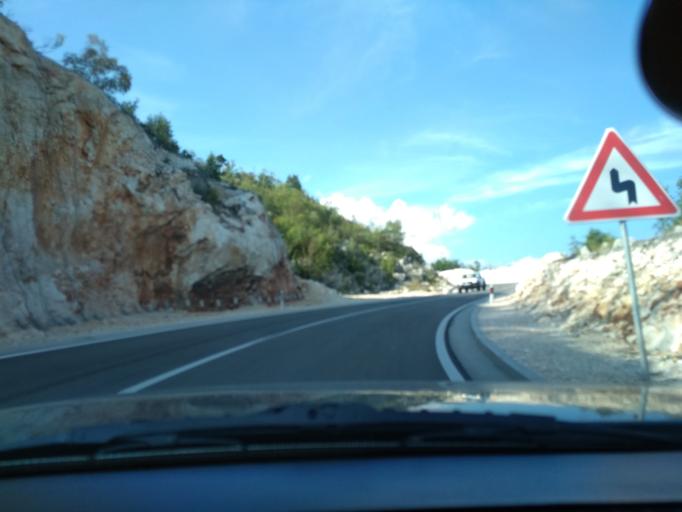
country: ME
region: Cetinje
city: Cetinje
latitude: 42.4056
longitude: 18.8879
